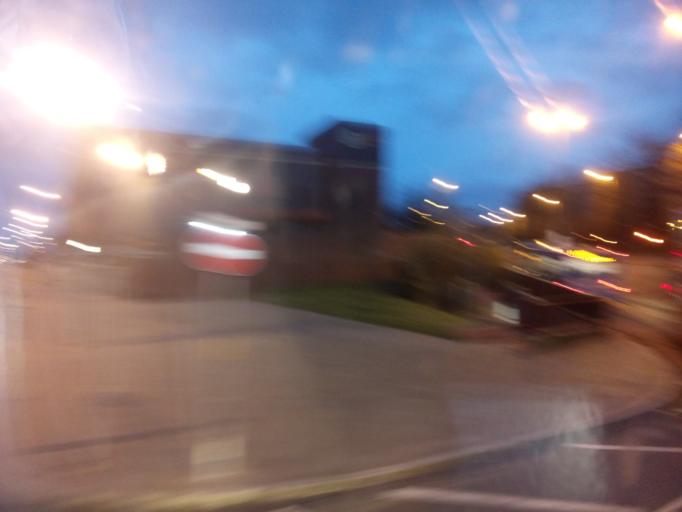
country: GB
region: England
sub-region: Gateshead
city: Gateshead
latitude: 54.9638
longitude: -1.6041
